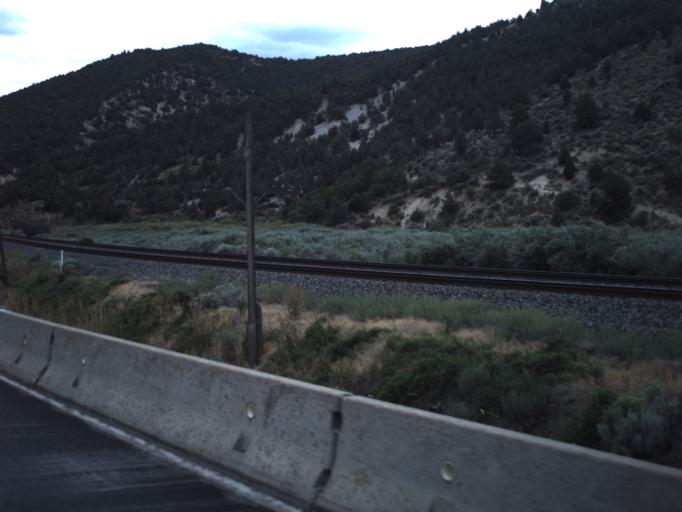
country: US
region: Utah
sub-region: Utah County
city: Mapleton
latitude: 39.9542
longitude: -111.2662
